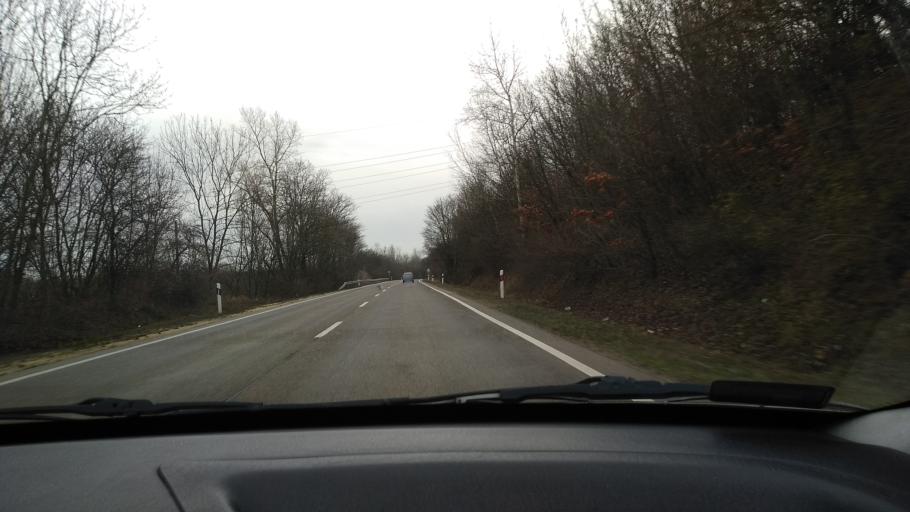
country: HU
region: Fejer
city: Szarliget
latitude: 47.5236
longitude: 18.4694
